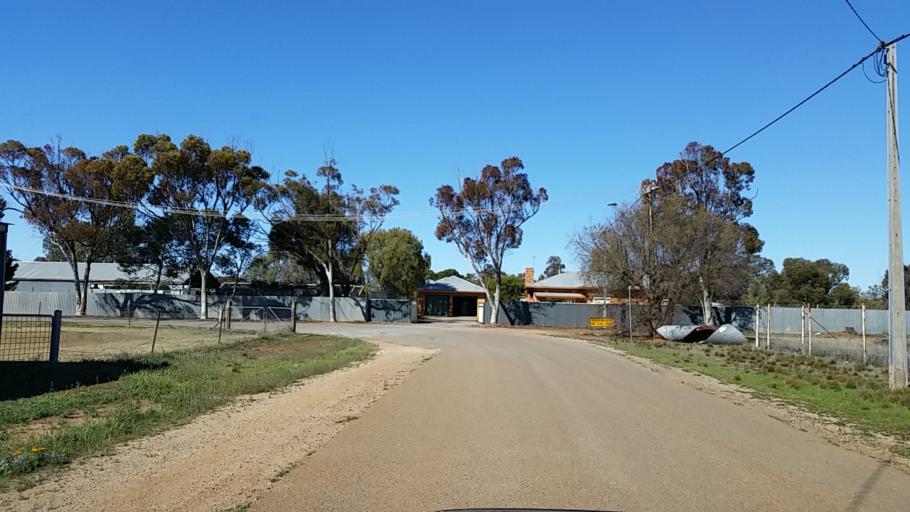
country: AU
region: South Australia
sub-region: Peterborough
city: Peterborough
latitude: -32.9786
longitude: 138.8423
